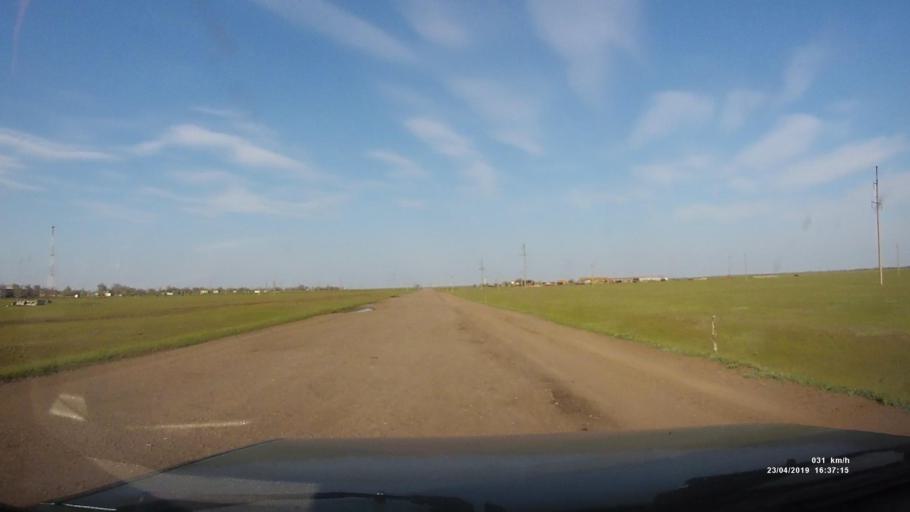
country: RU
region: Kalmykiya
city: Priyutnoye
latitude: 46.3321
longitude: 43.1461
